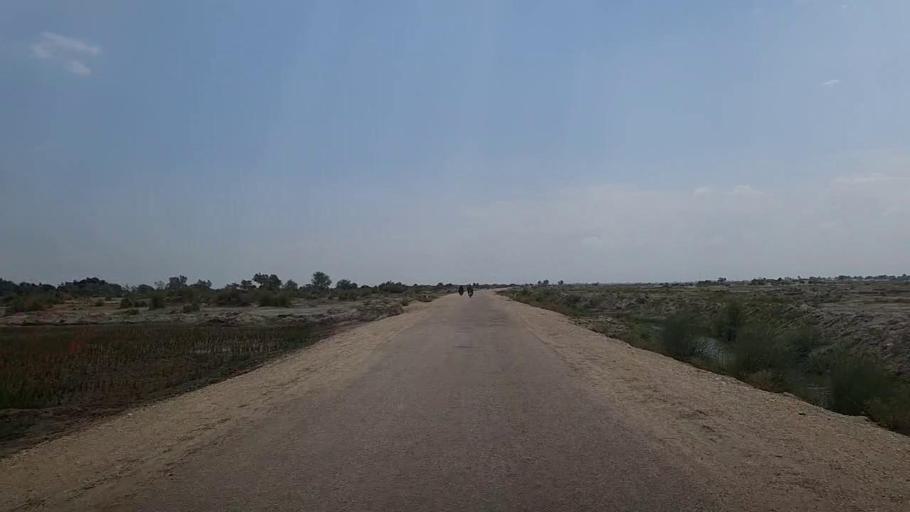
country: PK
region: Sindh
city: Kandhkot
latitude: 28.2924
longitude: 69.1406
